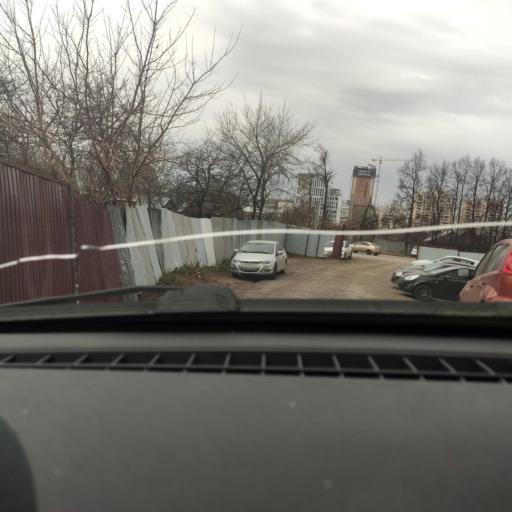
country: RU
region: Bashkortostan
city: Ufa
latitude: 54.7082
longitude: 55.9789
